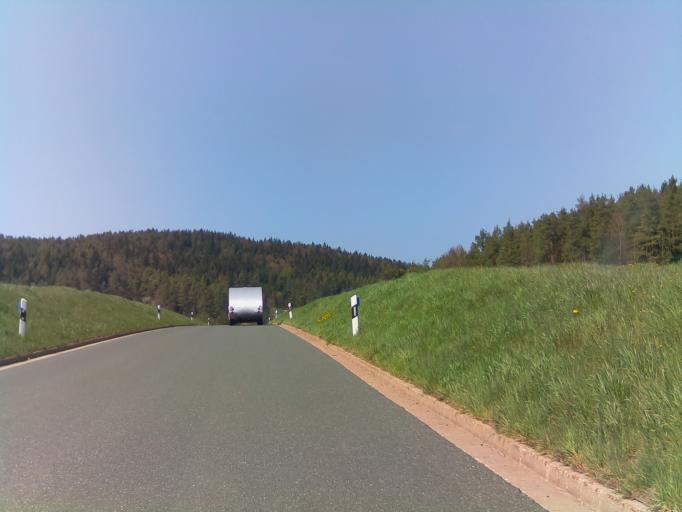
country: DE
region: Bavaria
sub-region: Upper Palatinate
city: Weigendorf
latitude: 49.4720
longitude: 11.5605
